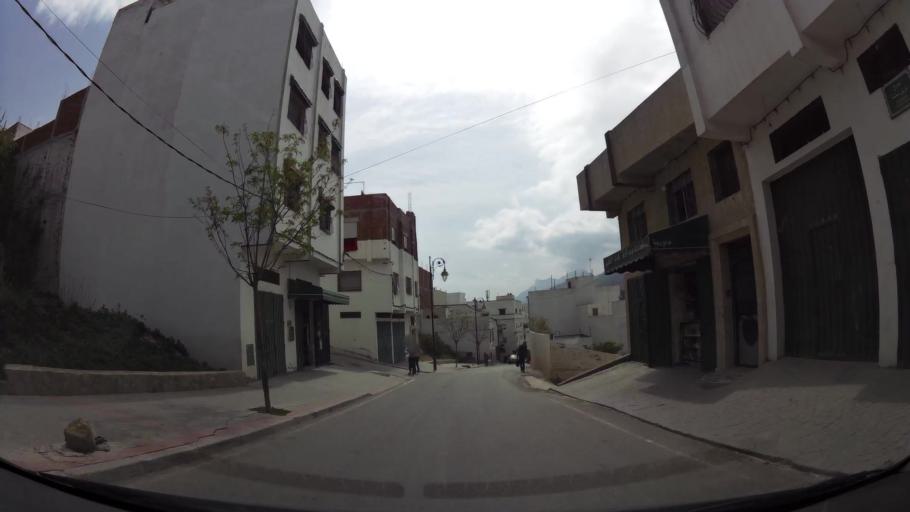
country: MA
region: Tanger-Tetouan
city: Tetouan
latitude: 35.5770
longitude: -5.3981
